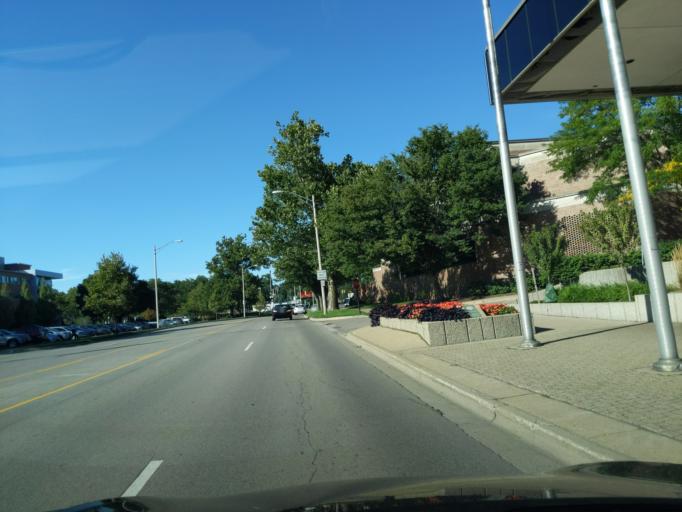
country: US
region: Michigan
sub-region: Ingham County
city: East Lansing
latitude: 42.7316
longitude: -84.4939
